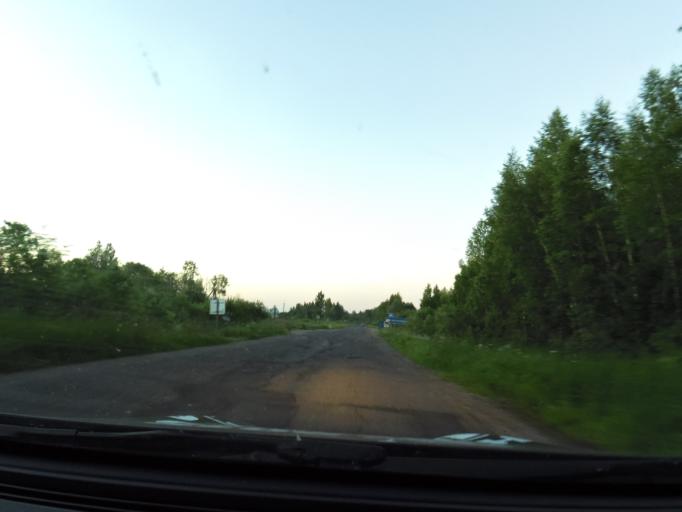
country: RU
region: Kostroma
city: Buy
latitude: 58.4392
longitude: 41.3355
